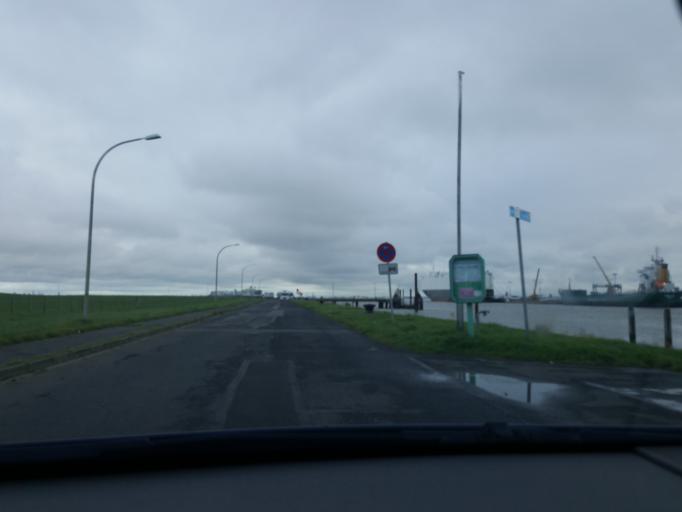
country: DE
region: Lower Saxony
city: Emden
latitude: 53.3398
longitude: 7.1858
